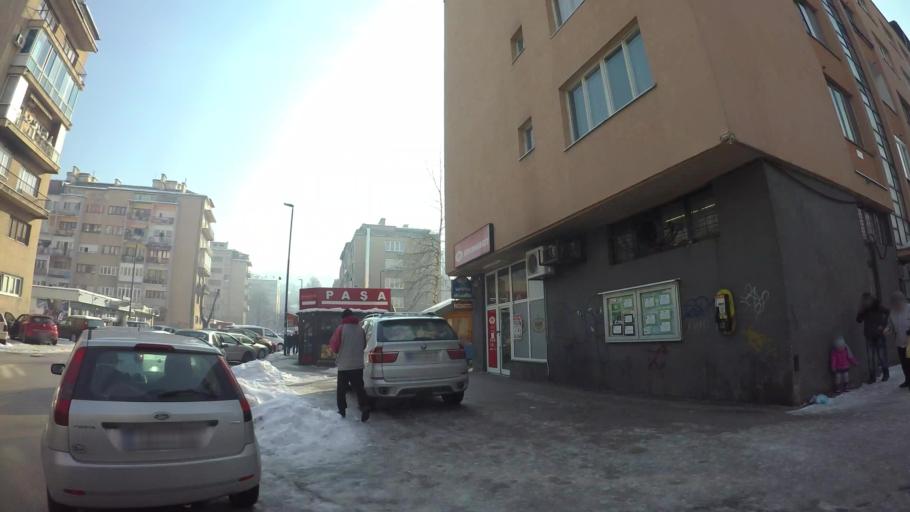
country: BA
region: Federation of Bosnia and Herzegovina
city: Kobilja Glava
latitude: 43.8511
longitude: 18.3953
